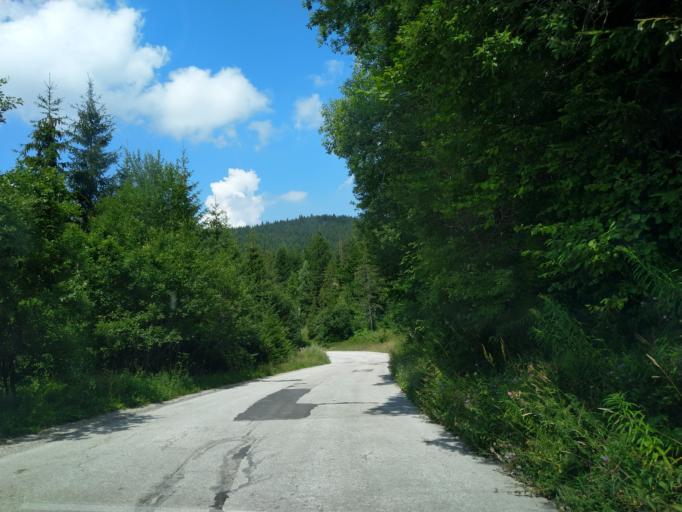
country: RS
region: Central Serbia
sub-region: Zlatiborski Okrug
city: Nova Varos
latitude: 43.5442
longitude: 19.9018
